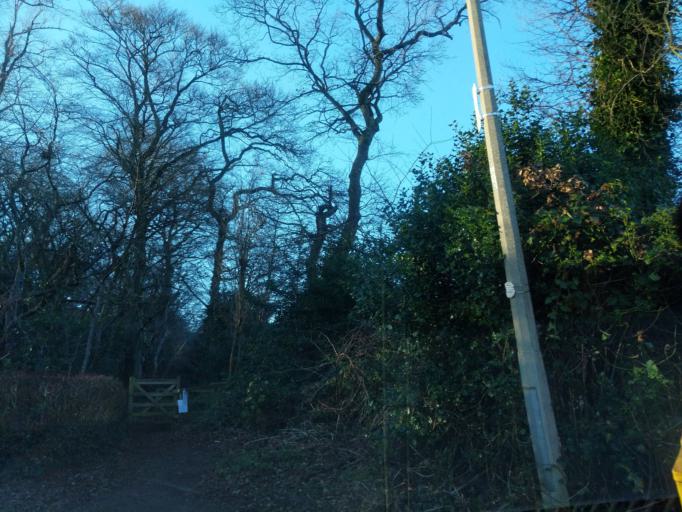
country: GB
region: Scotland
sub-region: Edinburgh
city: Colinton
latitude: 55.8998
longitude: -3.2520
